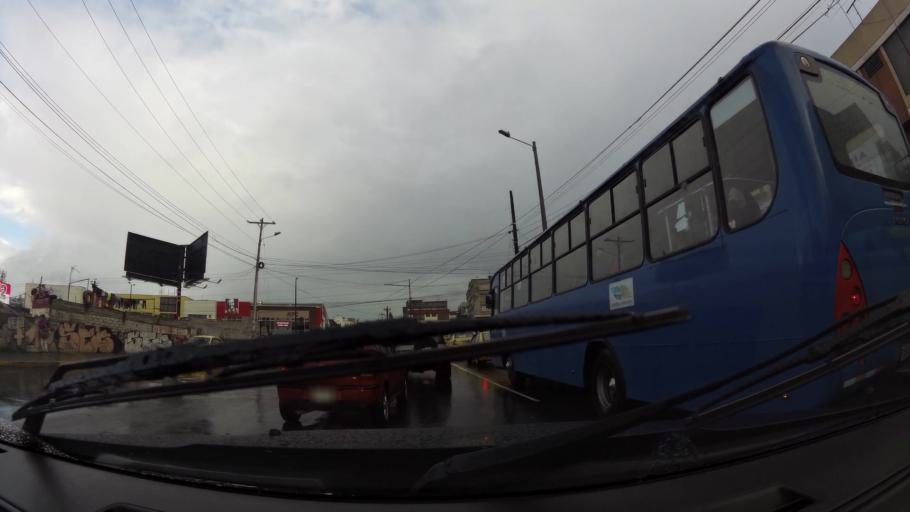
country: EC
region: Pichincha
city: Quito
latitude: -0.1049
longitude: -78.4978
